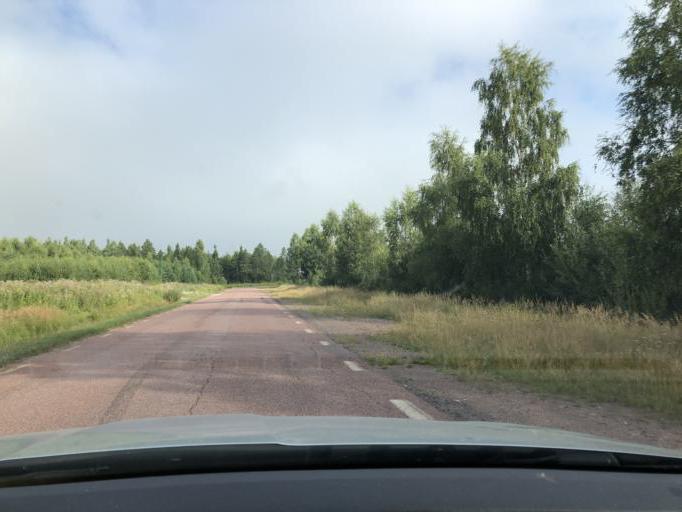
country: SE
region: Dalarna
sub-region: Mora Kommun
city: Mora
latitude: 60.9656
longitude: 14.4988
